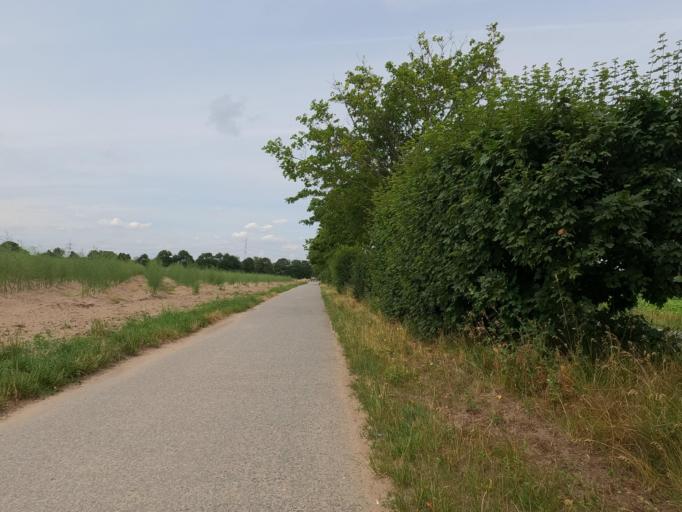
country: DE
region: Hesse
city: Weiterstadt
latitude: 49.9385
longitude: 8.6028
